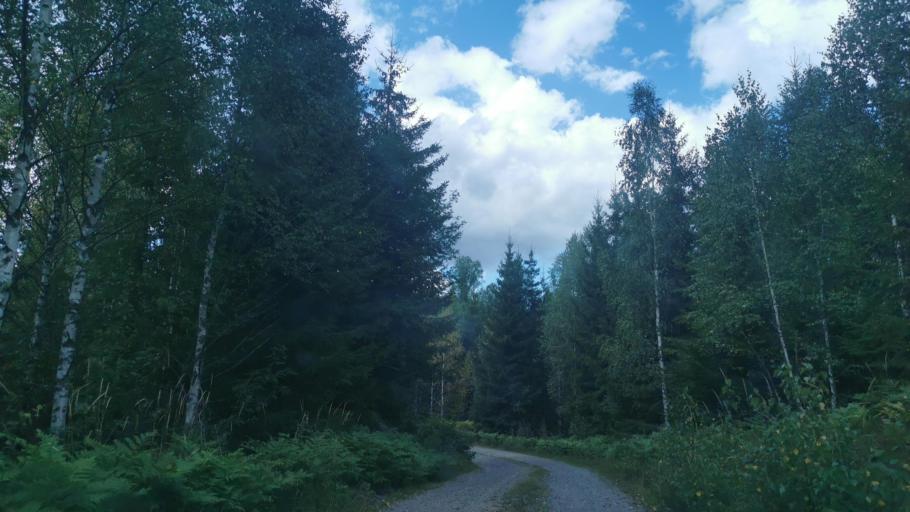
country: SE
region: OEstergoetland
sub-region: Finspangs Kommun
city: Finspang
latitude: 58.7999
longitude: 15.7844
